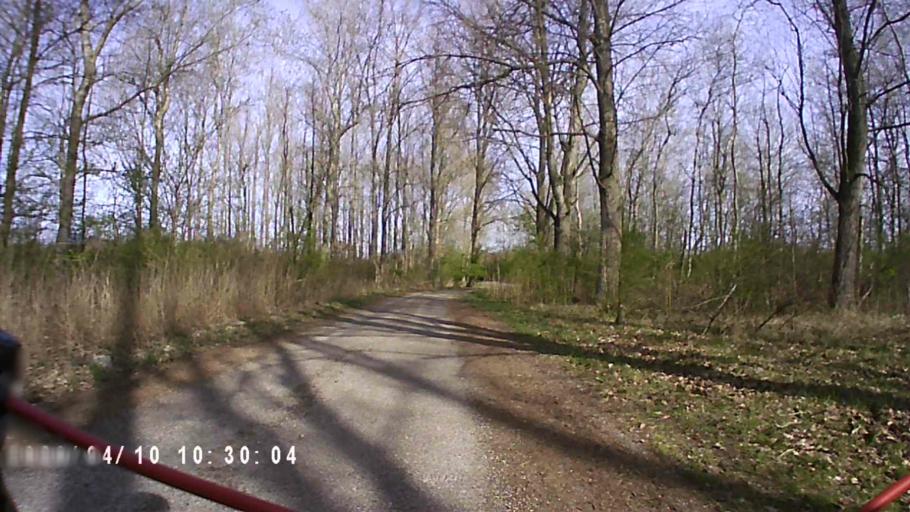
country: NL
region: Friesland
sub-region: Gemeente Dongeradeel
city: Anjum
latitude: 53.3919
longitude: 6.2125
